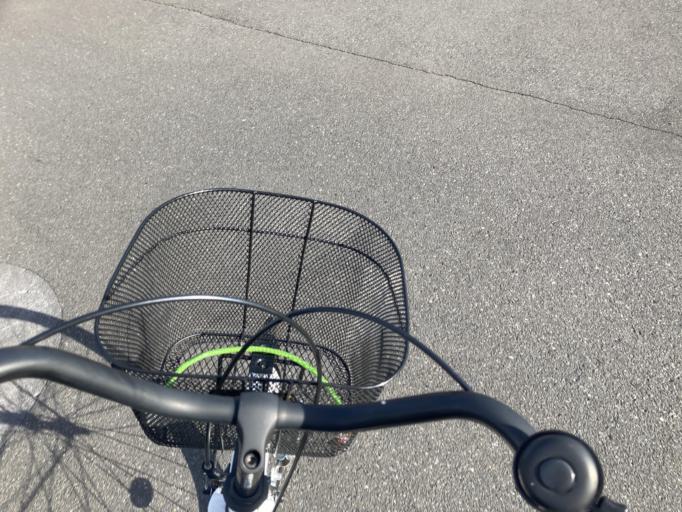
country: JP
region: Ibaraki
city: Naka
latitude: 36.0836
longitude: 140.0909
